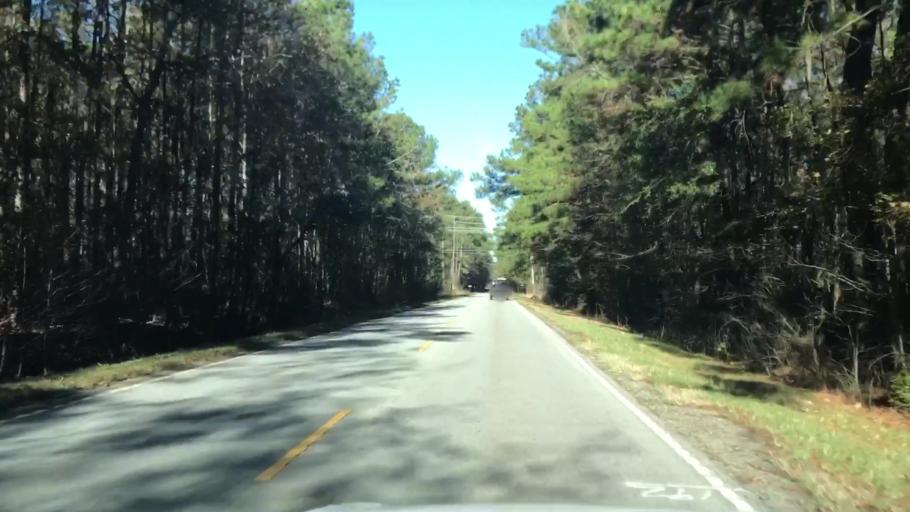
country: US
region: South Carolina
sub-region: Dorchester County
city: Centerville
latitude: 32.9168
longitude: -80.1566
